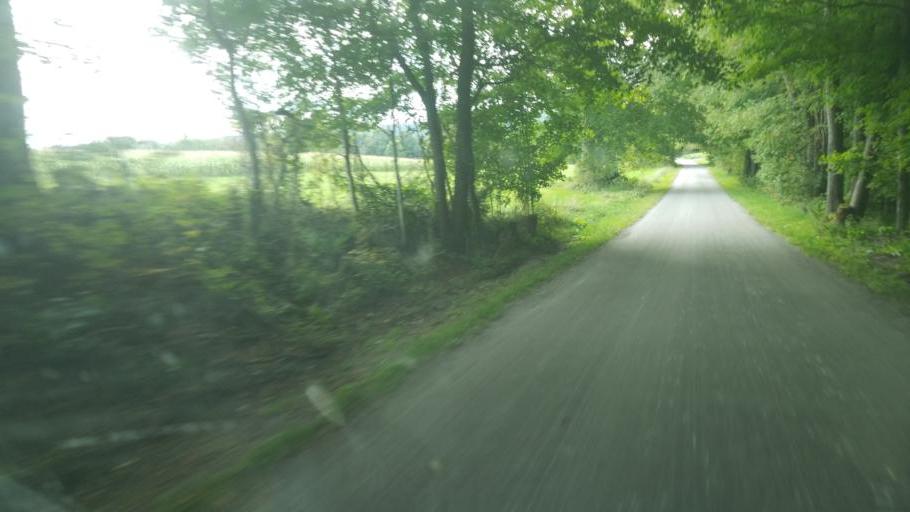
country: US
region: Pennsylvania
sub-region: Mercer County
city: Greenville
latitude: 41.4775
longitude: -80.3433
